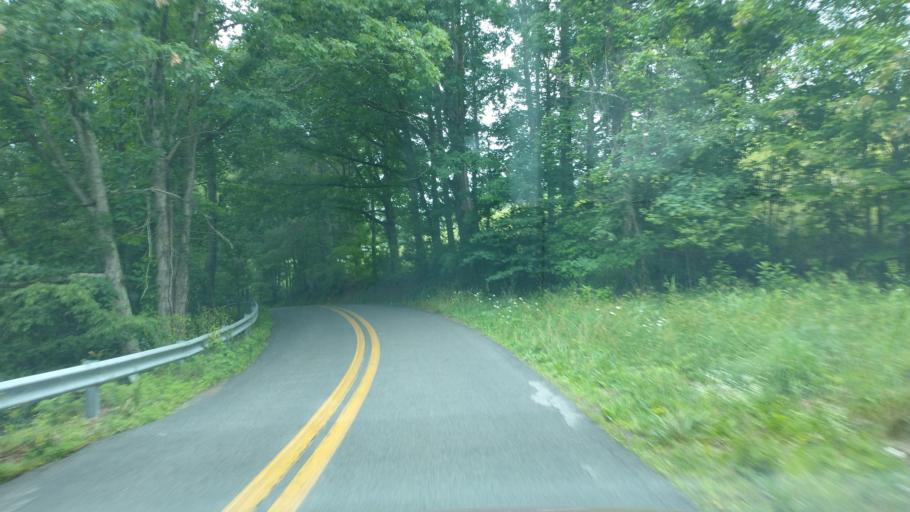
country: US
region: West Virginia
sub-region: Mercer County
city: Athens
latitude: 37.4353
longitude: -80.9696
